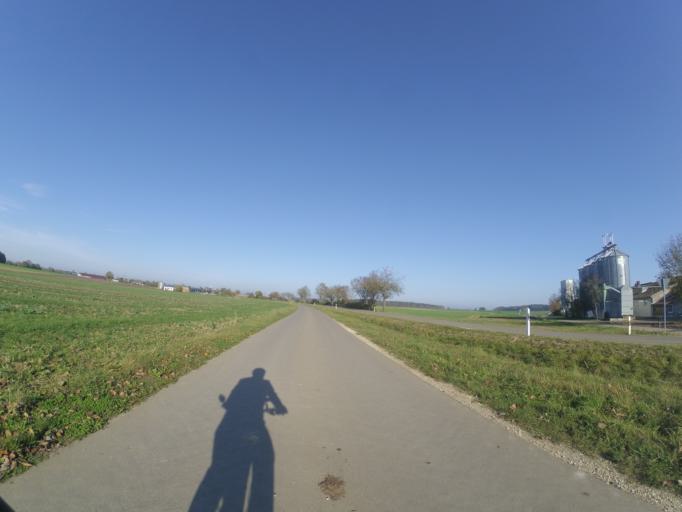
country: DE
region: Baden-Wuerttemberg
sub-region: Tuebingen Region
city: Blaubeuren
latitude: 48.4239
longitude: 9.8143
